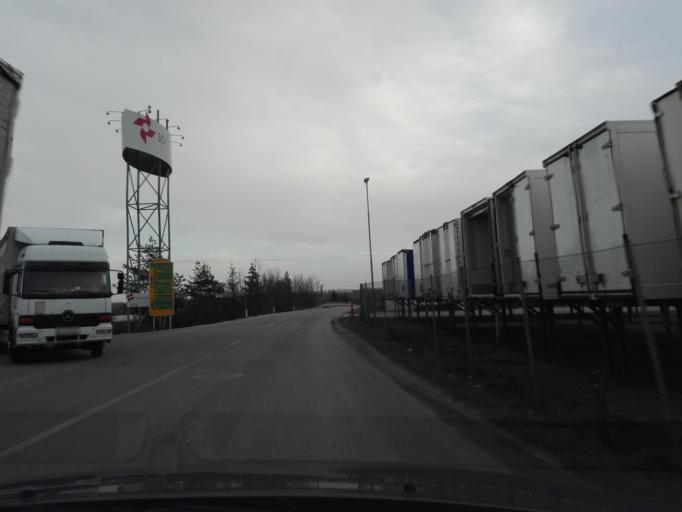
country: AT
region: Upper Austria
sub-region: Politischer Bezirk Linz-Land
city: Horsching
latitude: 48.2033
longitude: 14.1574
